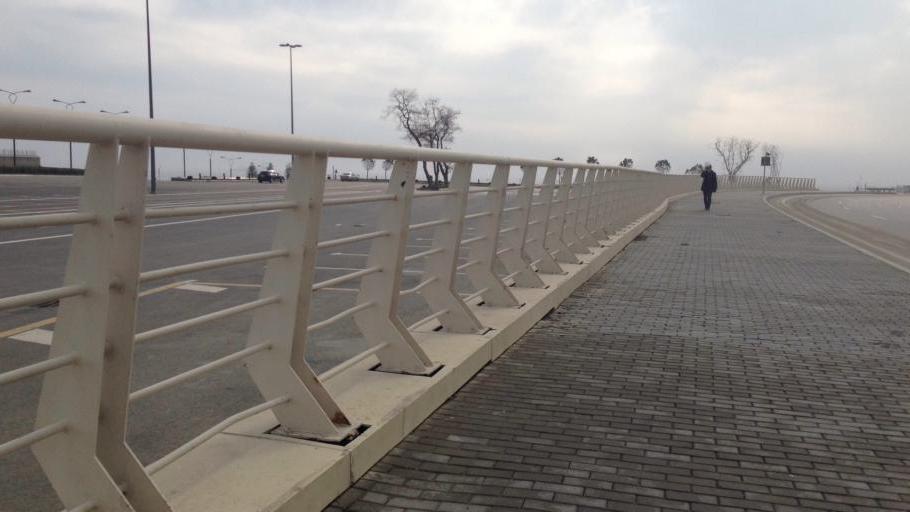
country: AZ
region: Baki
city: Badamdar
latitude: 40.3442
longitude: 49.8427
